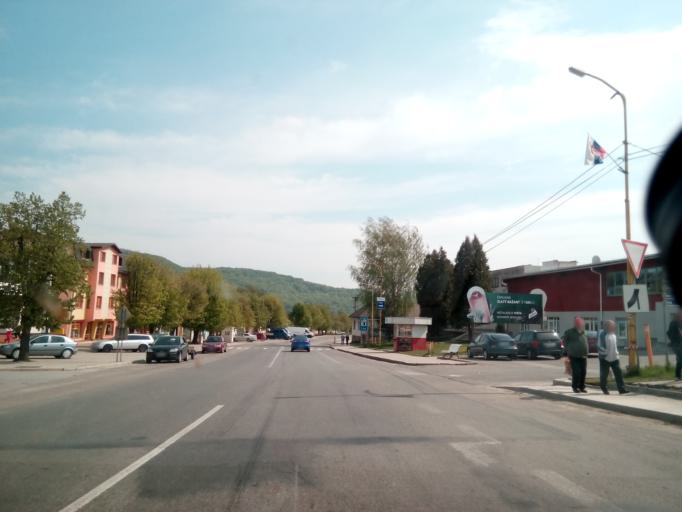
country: SK
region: Presovsky
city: Giraltovce
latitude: 49.0272
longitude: 21.5029
